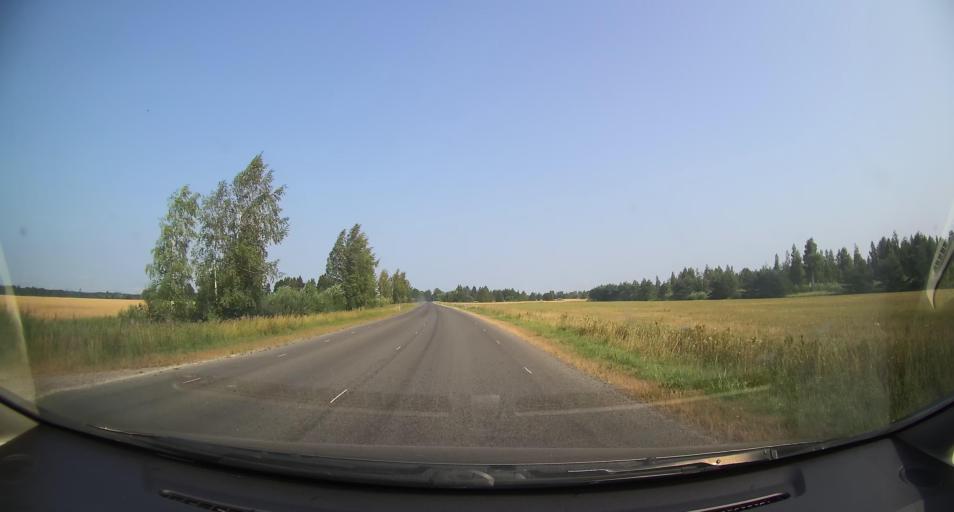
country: EE
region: Paernumaa
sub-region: Audru vald
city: Audru
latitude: 58.4563
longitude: 24.3174
